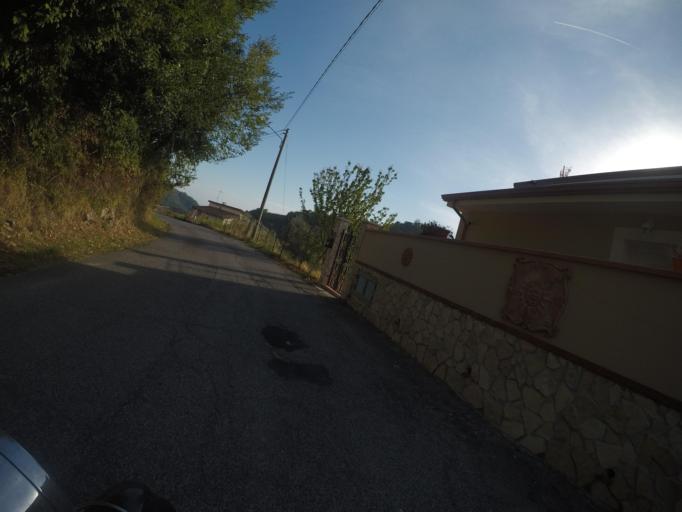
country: IT
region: Tuscany
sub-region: Provincia di Massa-Carrara
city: Carrara
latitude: 44.0870
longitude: 10.0897
